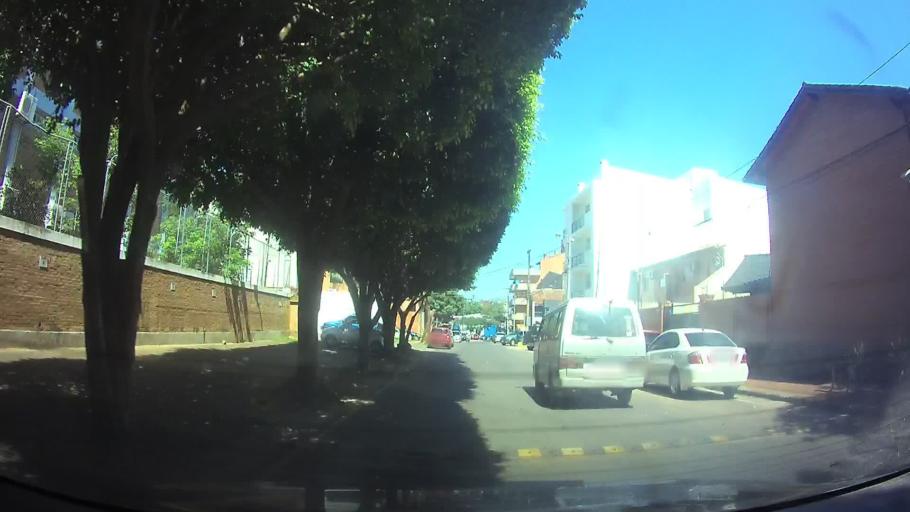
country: PY
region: Central
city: Fernando de la Mora
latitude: -25.3114
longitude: -57.5288
